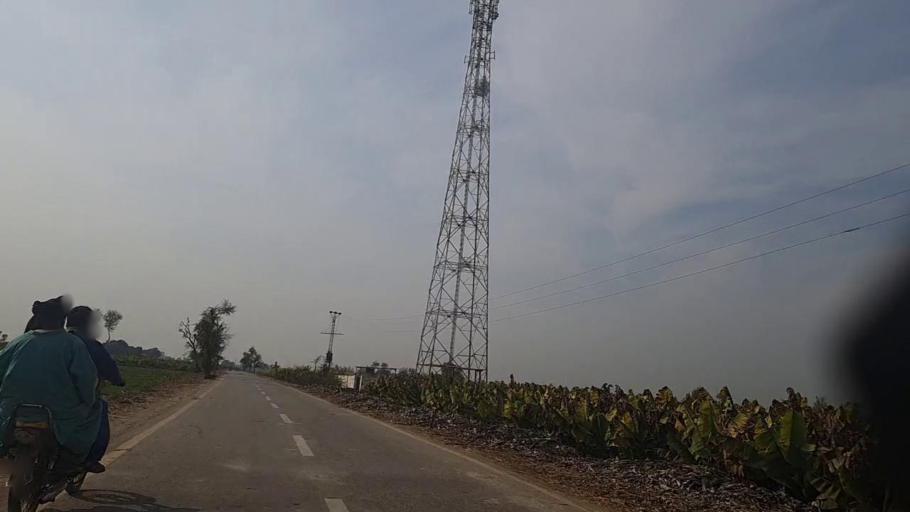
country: PK
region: Sindh
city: Daur
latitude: 26.4048
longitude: 68.2358
